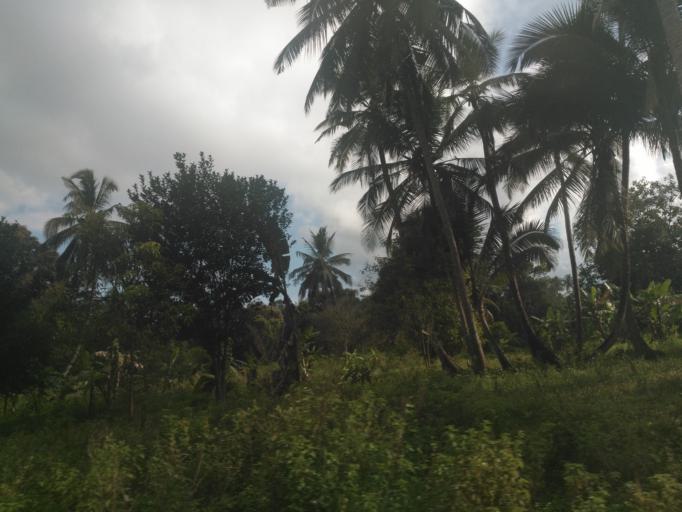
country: TZ
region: Zanzibar Central/South
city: Koani
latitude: -6.1072
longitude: 39.2963
